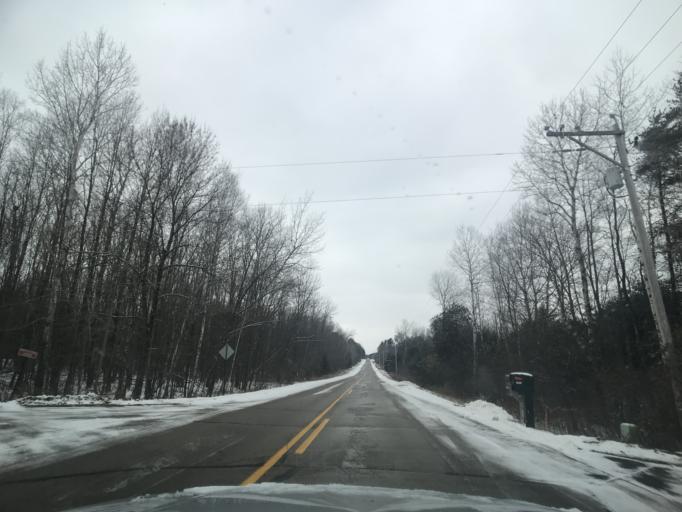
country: US
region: Wisconsin
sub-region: Brown County
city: Suamico
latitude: 44.7063
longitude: -88.0939
